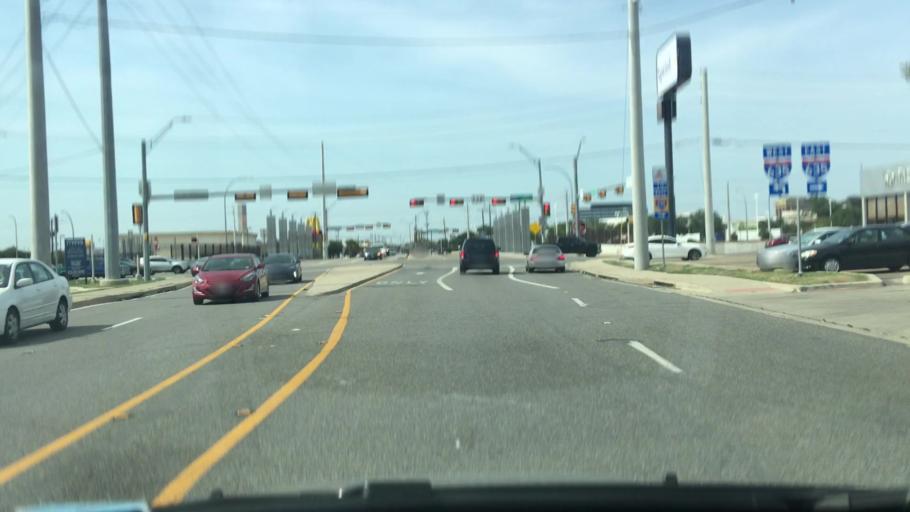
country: US
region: Texas
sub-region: Dallas County
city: Addison
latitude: 32.9248
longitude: -96.8112
